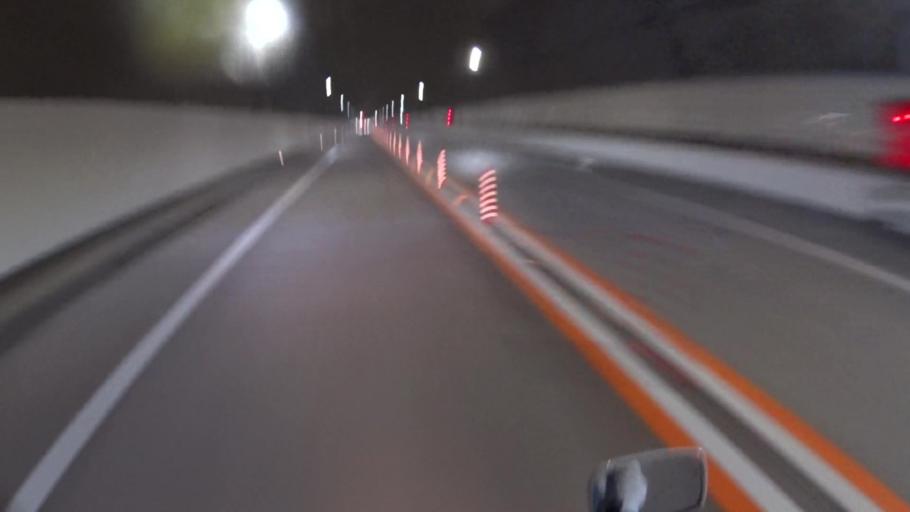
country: JP
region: Kyoto
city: Ayabe
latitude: 35.2423
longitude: 135.3437
